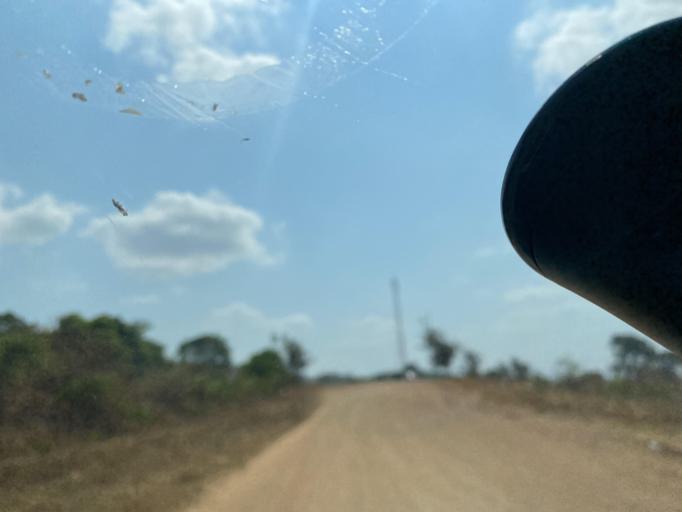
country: ZM
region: Lusaka
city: Chongwe
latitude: -15.6026
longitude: 28.7382
